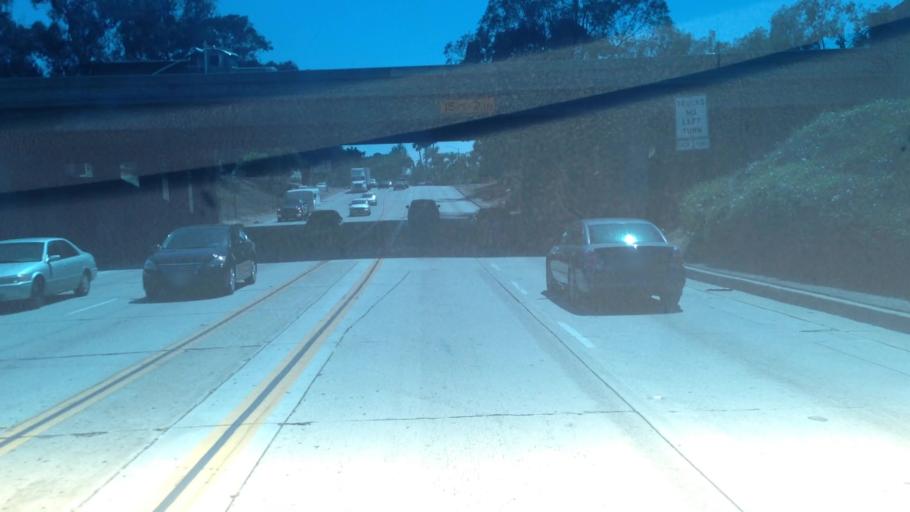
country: US
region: California
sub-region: Los Angeles County
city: Downey
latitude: 33.9647
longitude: -118.1196
